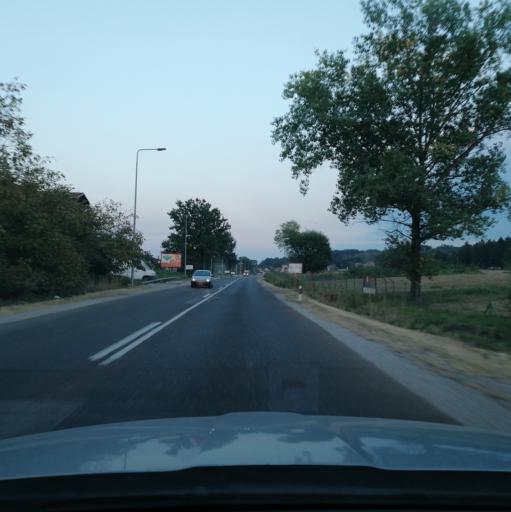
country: RS
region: Central Serbia
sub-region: Raski Okrug
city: Kraljevo
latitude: 43.7039
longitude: 20.7128
